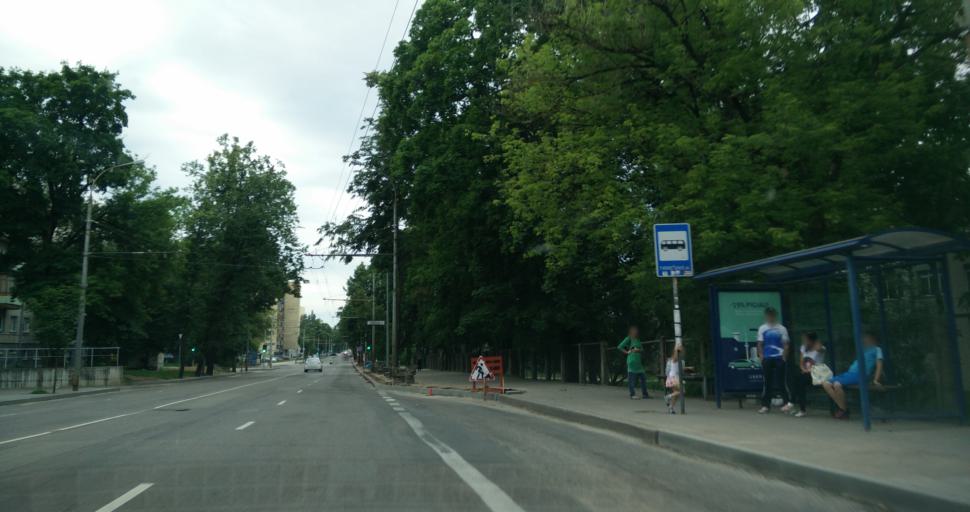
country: LT
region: Vilnius County
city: Rasos
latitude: 54.7176
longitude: 25.3167
